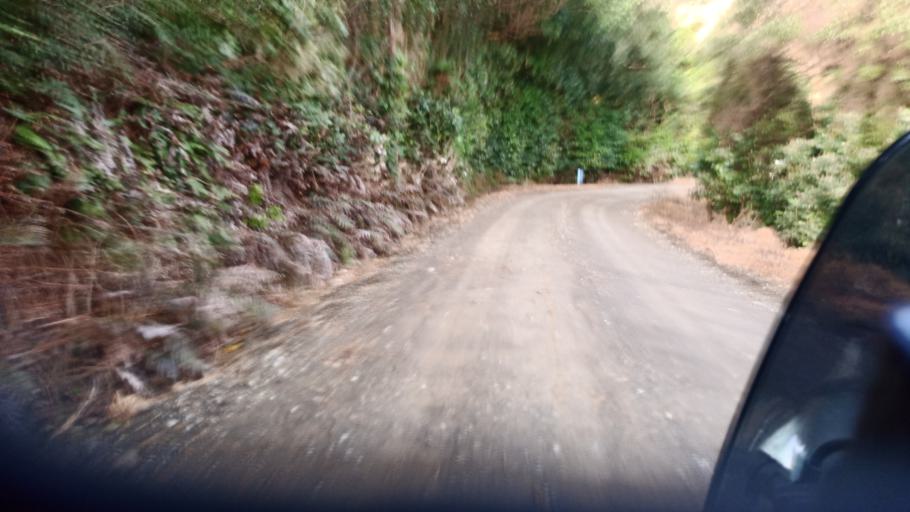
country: NZ
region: Gisborne
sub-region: Gisborne District
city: Gisborne
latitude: -38.4603
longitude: 177.5386
